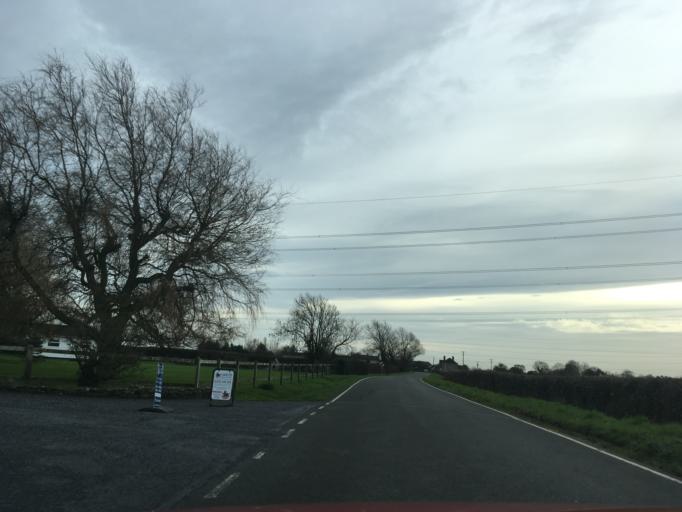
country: GB
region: Wales
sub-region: Monmouthshire
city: Magor
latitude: 51.5699
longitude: -2.8212
